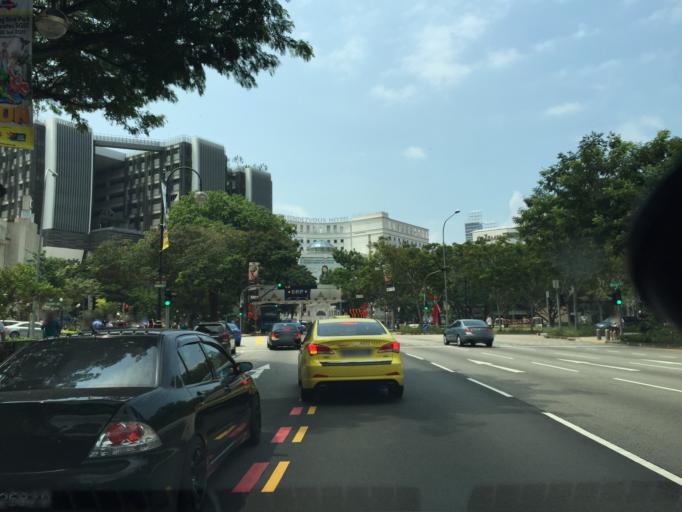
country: SG
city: Singapore
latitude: 1.2988
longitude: 103.8468
